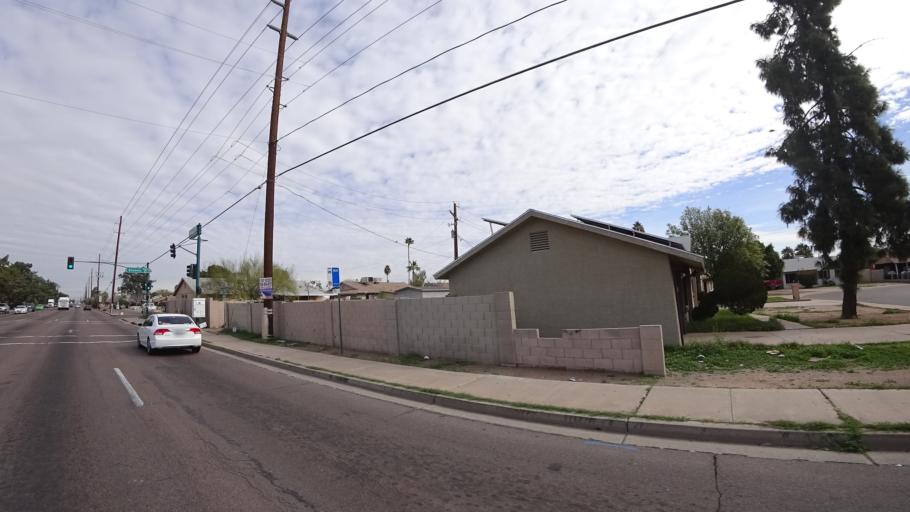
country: US
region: Arizona
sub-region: Maricopa County
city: Glendale
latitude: 33.4728
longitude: -112.1690
